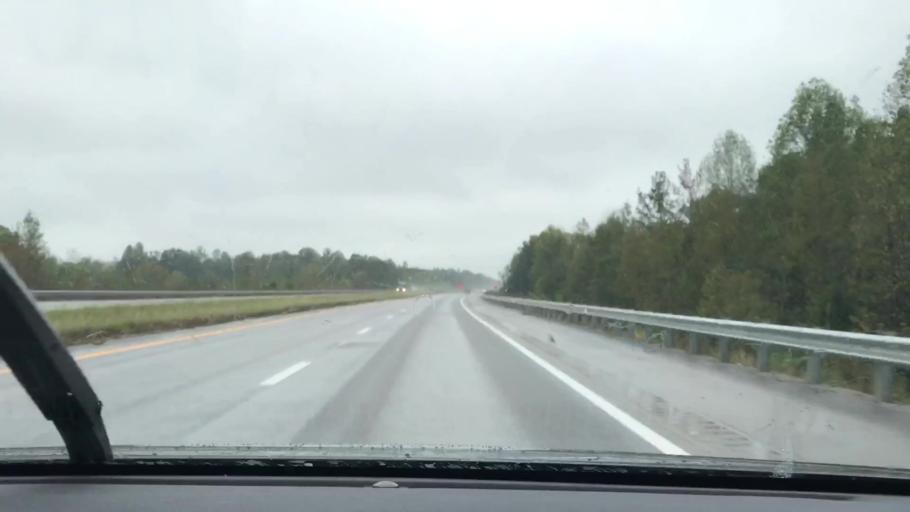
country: US
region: Kentucky
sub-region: Hopkins County
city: Nortonville
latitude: 37.1738
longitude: -87.4490
